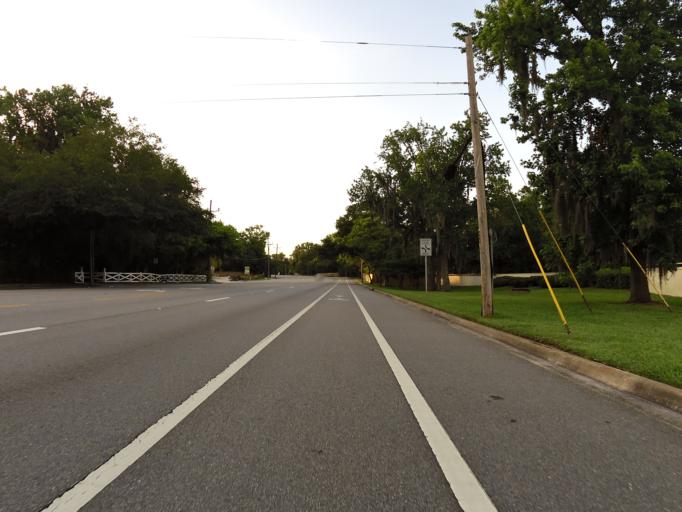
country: US
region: Florida
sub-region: Duval County
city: Jacksonville
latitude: 30.2301
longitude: -81.6168
